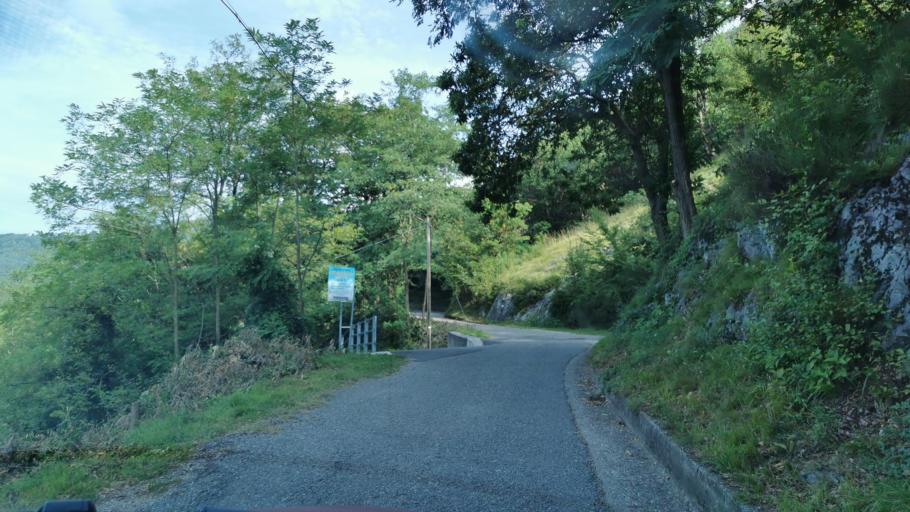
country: IT
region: Lombardy
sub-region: Provincia di Como
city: Vercana
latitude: 46.1637
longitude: 9.3282
